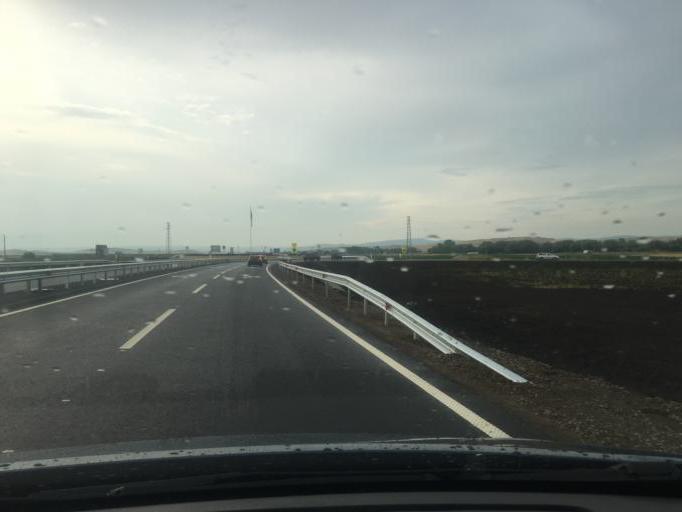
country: BG
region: Burgas
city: Aheloy
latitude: 42.6443
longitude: 27.6372
